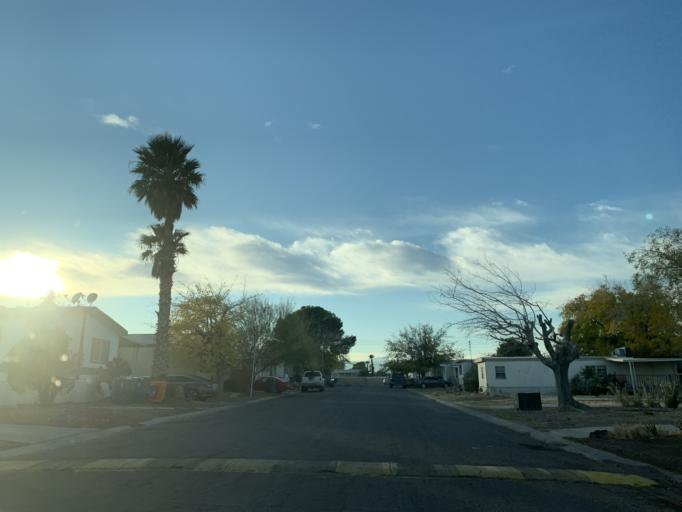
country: US
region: Nevada
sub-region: Clark County
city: Spring Valley
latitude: 36.1030
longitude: -115.2234
